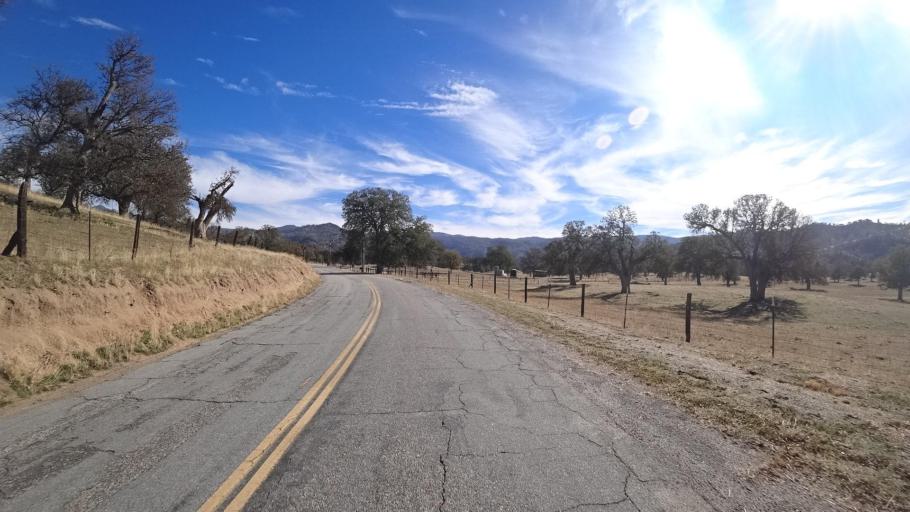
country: US
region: California
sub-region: Kern County
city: Alta Sierra
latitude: 35.6225
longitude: -118.7450
